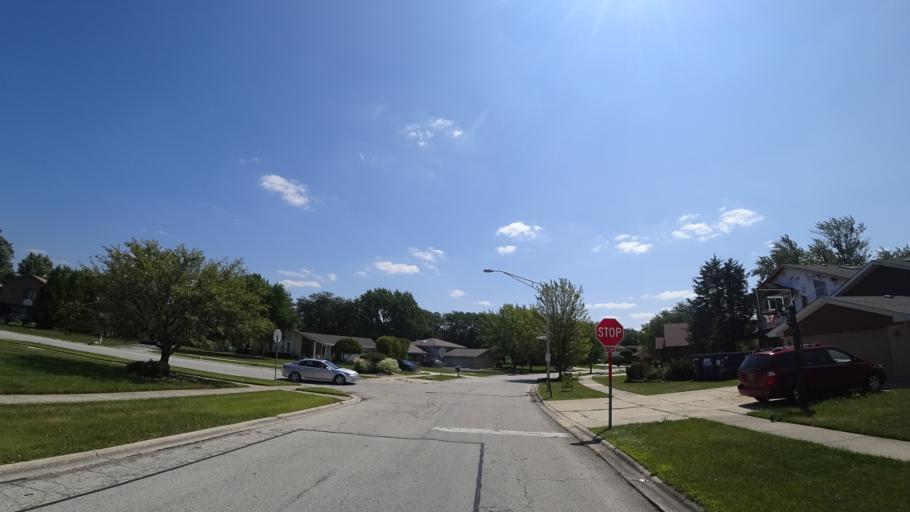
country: US
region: Illinois
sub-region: Cook County
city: Orland Park
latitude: 41.6191
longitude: -87.8350
